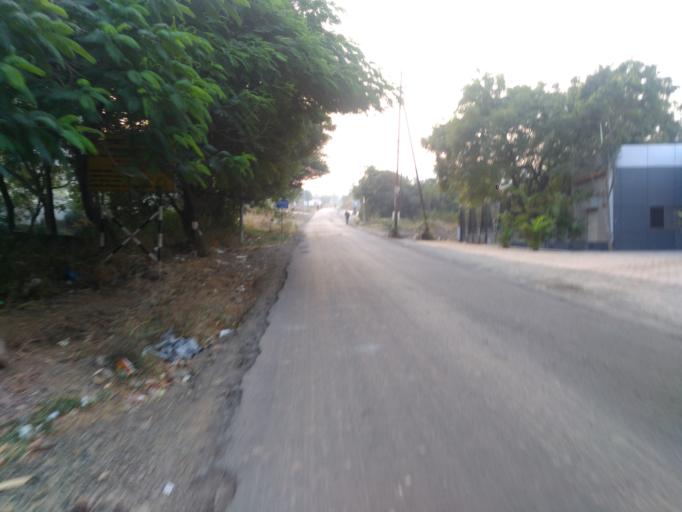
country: IN
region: Maharashtra
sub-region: Pune Division
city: Pune
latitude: 18.4284
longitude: 73.8997
